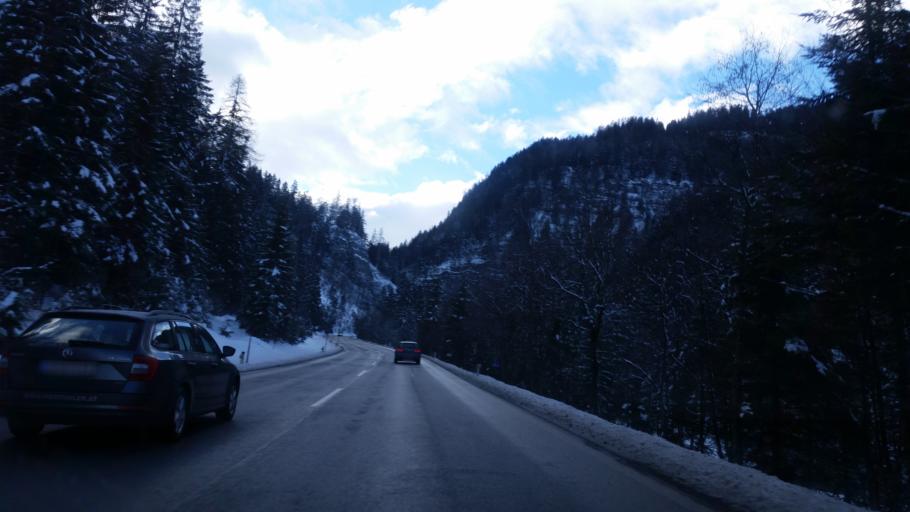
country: AT
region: Salzburg
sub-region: Politischer Bezirk Sankt Johann im Pongau
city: Untertauern
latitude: 47.2983
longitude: 13.5057
